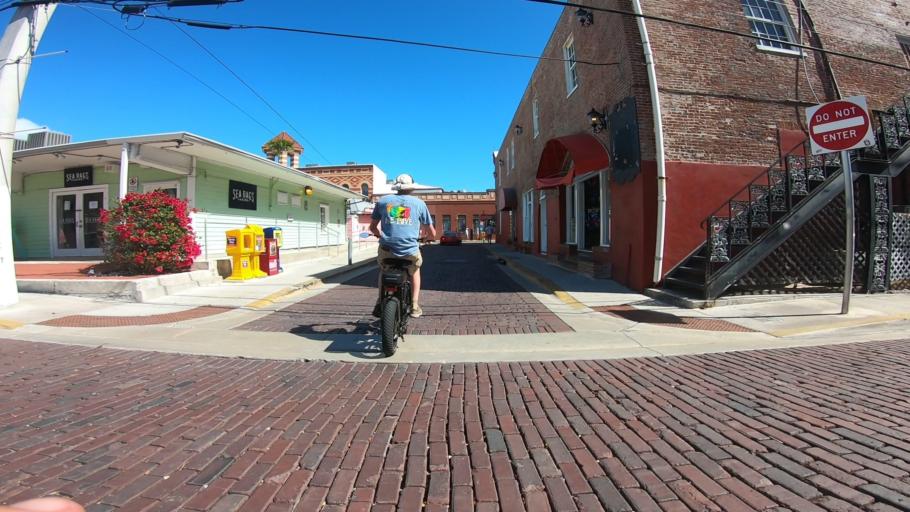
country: US
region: Florida
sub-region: Monroe County
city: Key West
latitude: 24.5601
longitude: -81.8070
